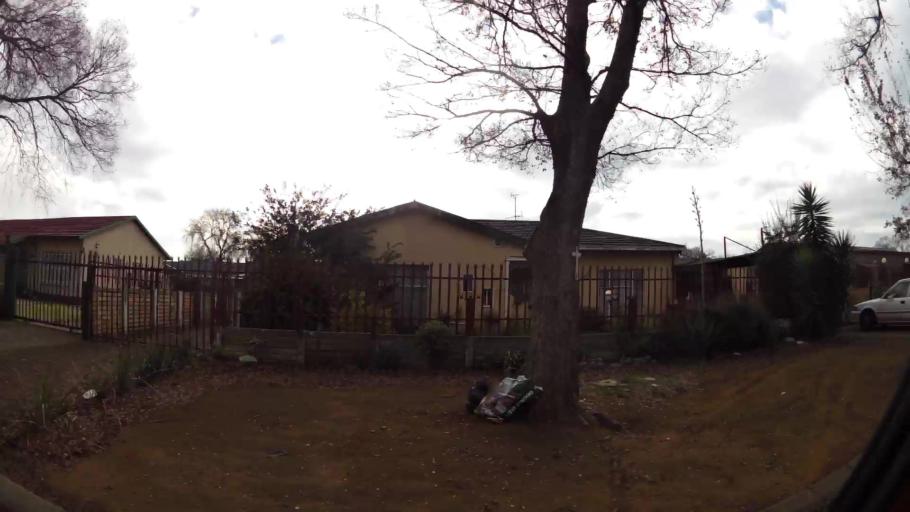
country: ZA
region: Gauteng
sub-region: Sedibeng District Municipality
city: Vanderbijlpark
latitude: -26.6918
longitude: 27.8249
